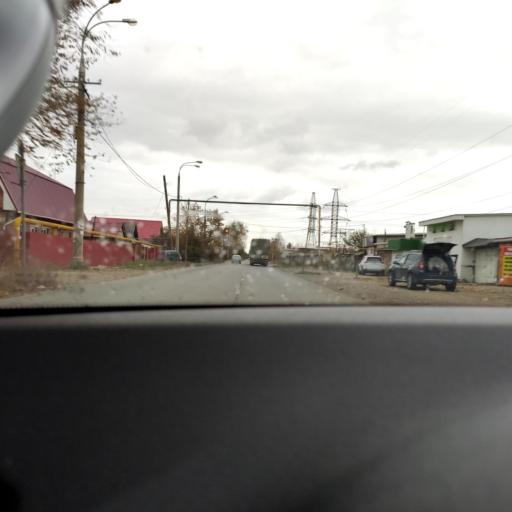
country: RU
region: Samara
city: Smyshlyayevka
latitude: 53.2323
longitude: 50.3141
